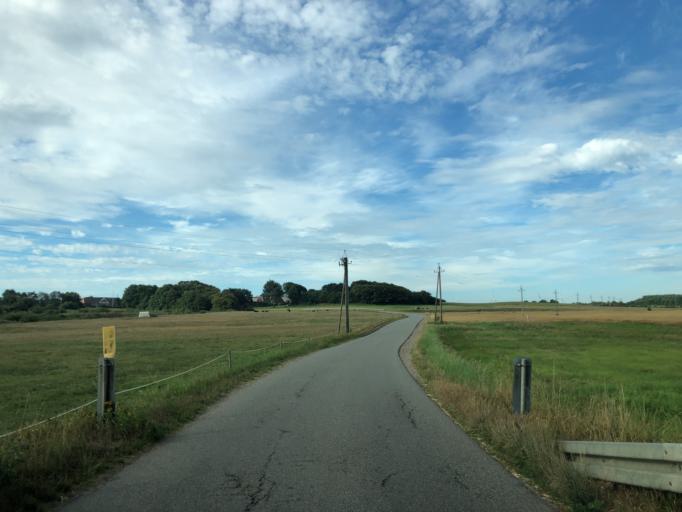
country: DK
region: Central Jutland
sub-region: Holstebro Kommune
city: Ulfborg
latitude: 56.1419
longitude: 8.4077
